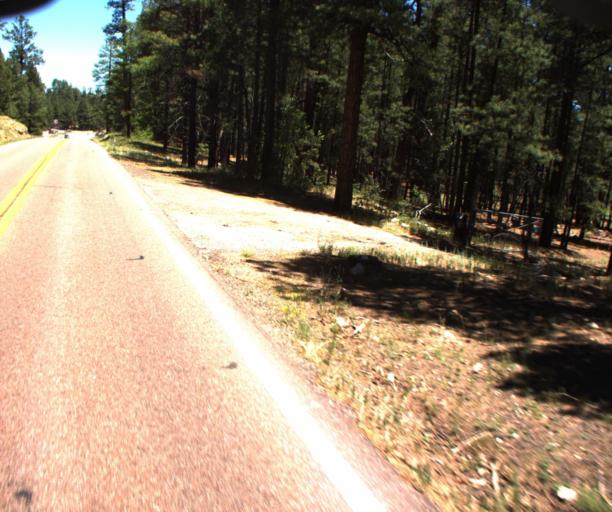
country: US
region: Arizona
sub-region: Gila County
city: Pine
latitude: 34.5430
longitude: -111.3249
